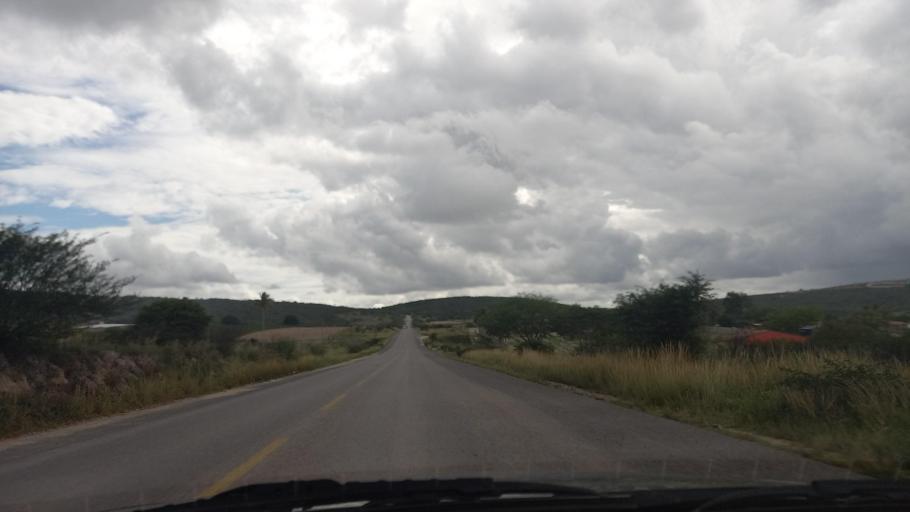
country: BR
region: Pernambuco
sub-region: Lajedo
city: Lajedo
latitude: -8.6704
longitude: -36.3837
